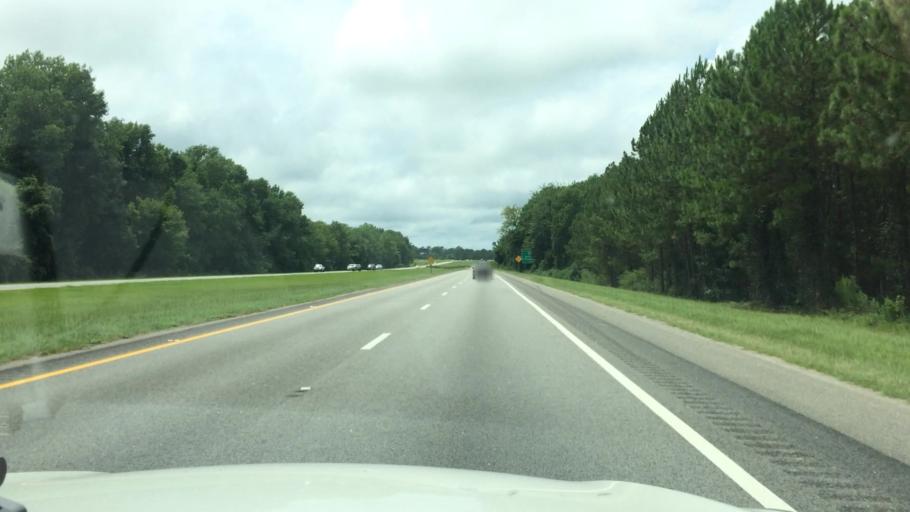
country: US
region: South Carolina
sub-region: Florence County
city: Timmonsville
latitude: 34.2036
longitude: -79.8891
